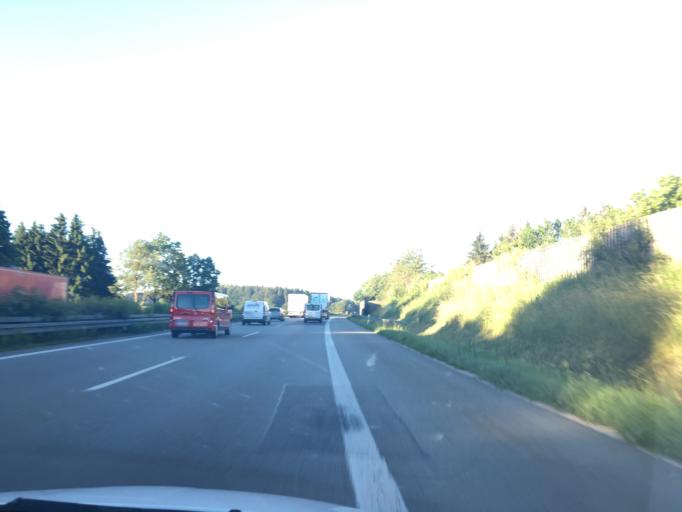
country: DE
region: Bavaria
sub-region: Swabia
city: Altenstadt
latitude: 48.1644
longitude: 10.1316
